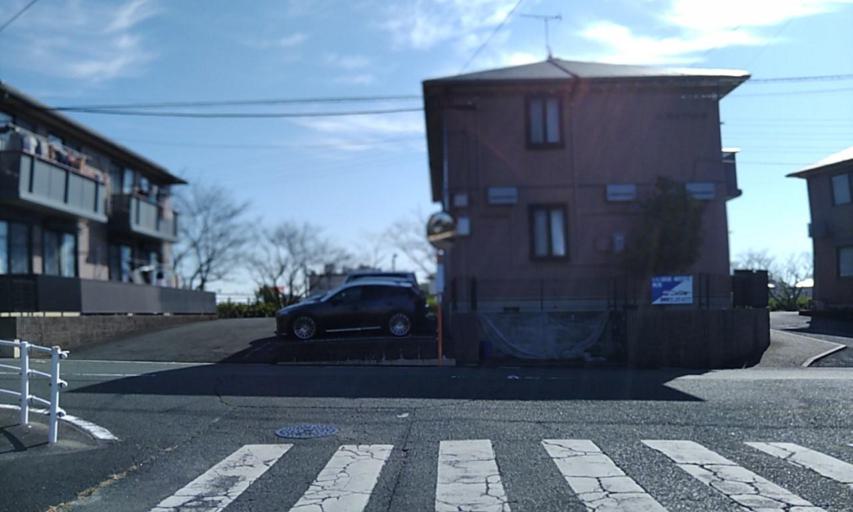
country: JP
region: Aichi
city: Tahara
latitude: 34.6706
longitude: 137.2749
